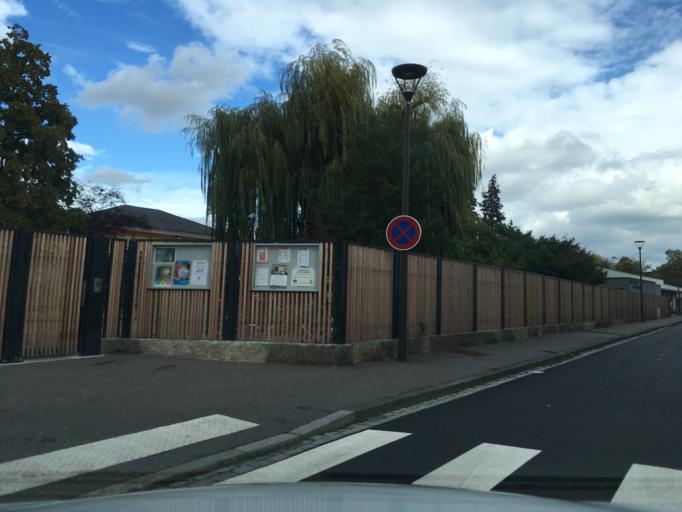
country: FR
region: Alsace
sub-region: Departement du Bas-Rhin
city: Schiltigheim
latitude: 48.5946
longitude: 7.7607
